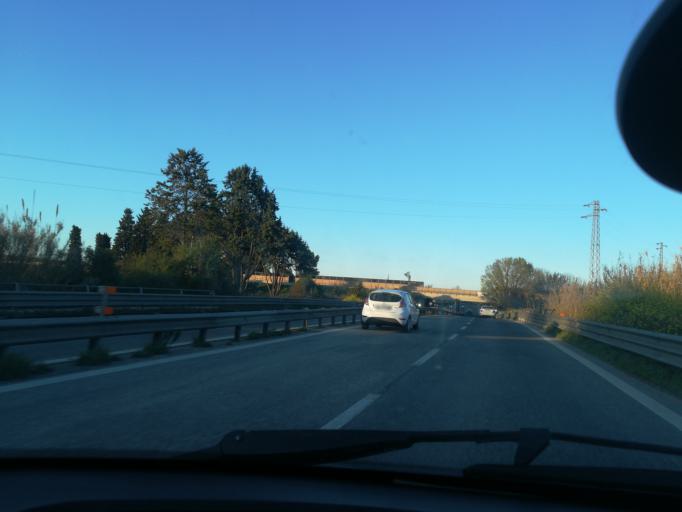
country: IT
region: The Marches
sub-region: Provincia di Macerata
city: Civitanova Marche
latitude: 43.2907
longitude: 13.7132
